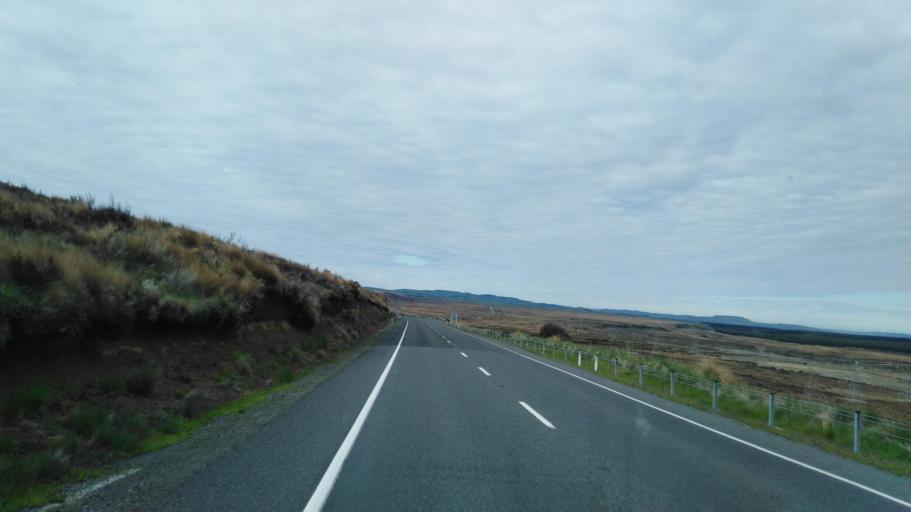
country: NZ
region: Manawatu-Wanganui
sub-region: Ruapehu District
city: Waiouru
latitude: -39.3801
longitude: 175.7105
